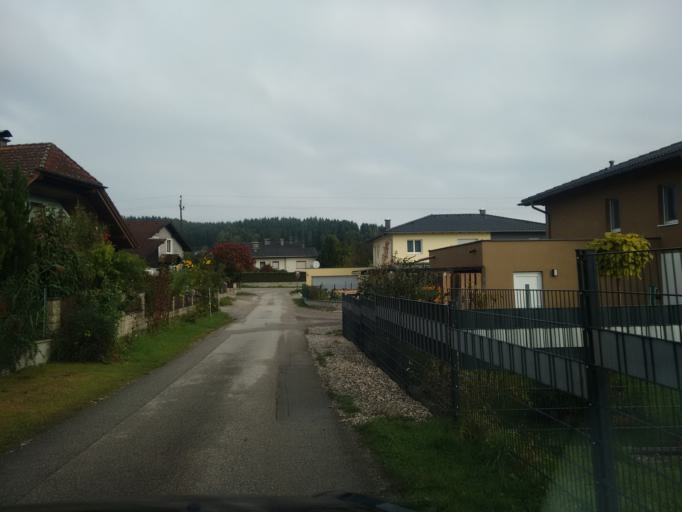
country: AT
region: Upper Austria
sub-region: Wels-Land
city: Buchkirchen
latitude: 48.1925
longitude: 13.9695
